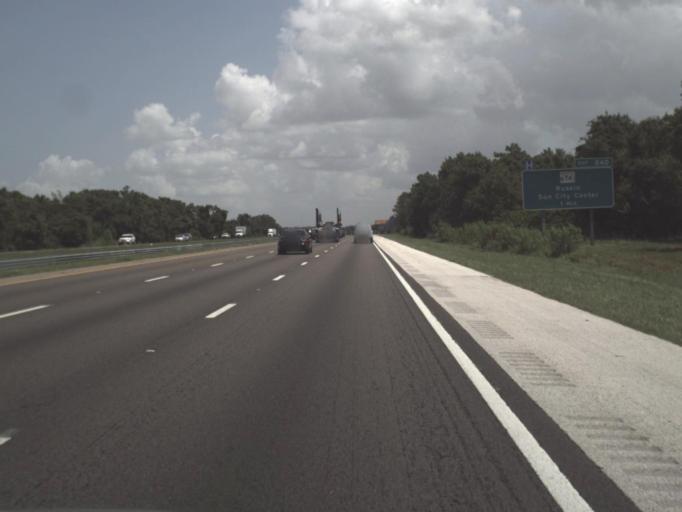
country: US
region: Florida
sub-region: Hillsborough County
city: Ruskin
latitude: 27.6986
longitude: -82.4015
